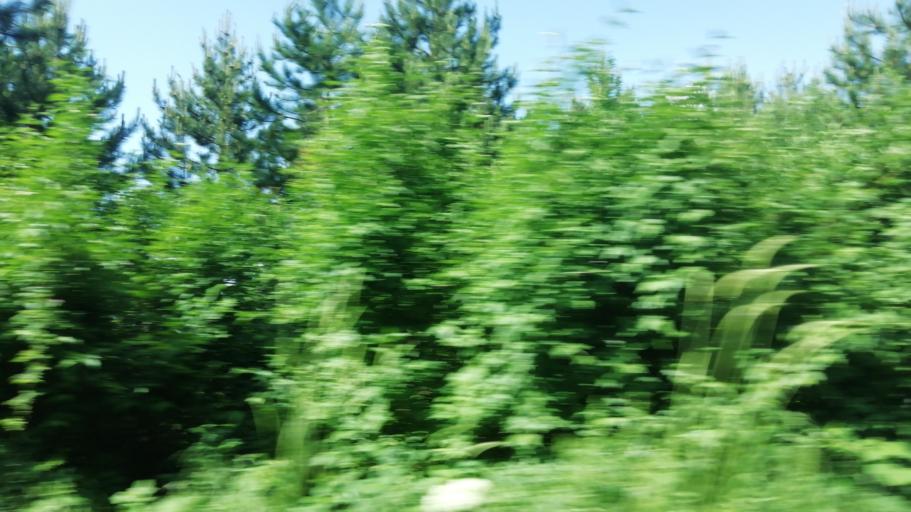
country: TR
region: Karabuk
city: Karabuk
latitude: 41.1246
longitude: 32.5889
